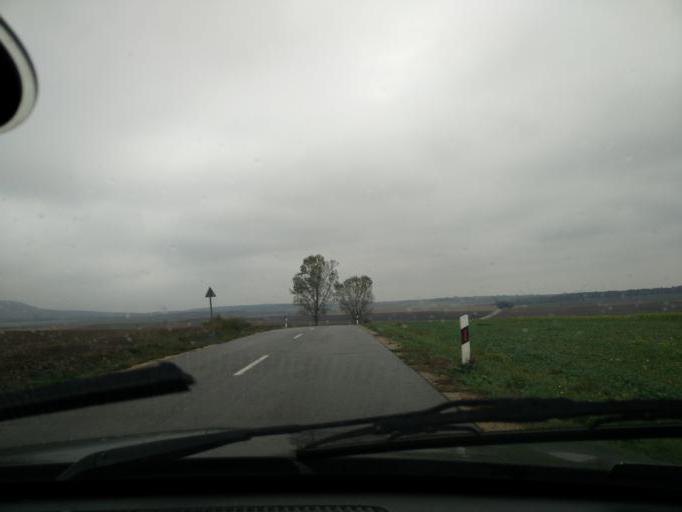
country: HU
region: Komarom-Esztergom
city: Bajna
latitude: 47.6407
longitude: 18.5708
